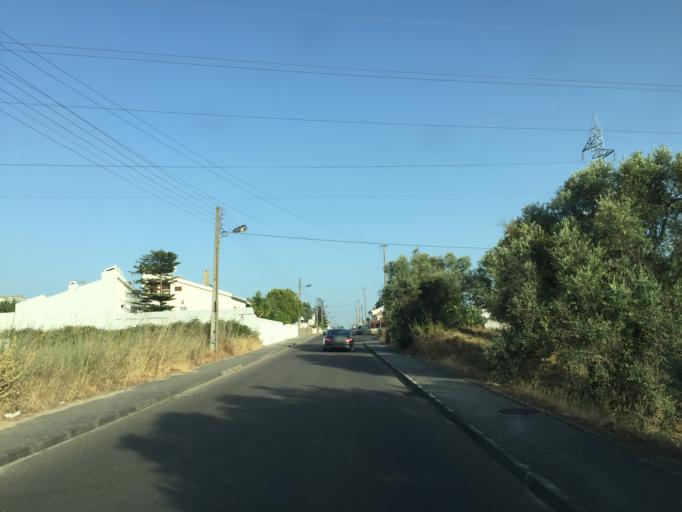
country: PT
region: Santarem
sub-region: Entroncamento
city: Entroncamento
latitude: 39.4741
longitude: -8.4478
